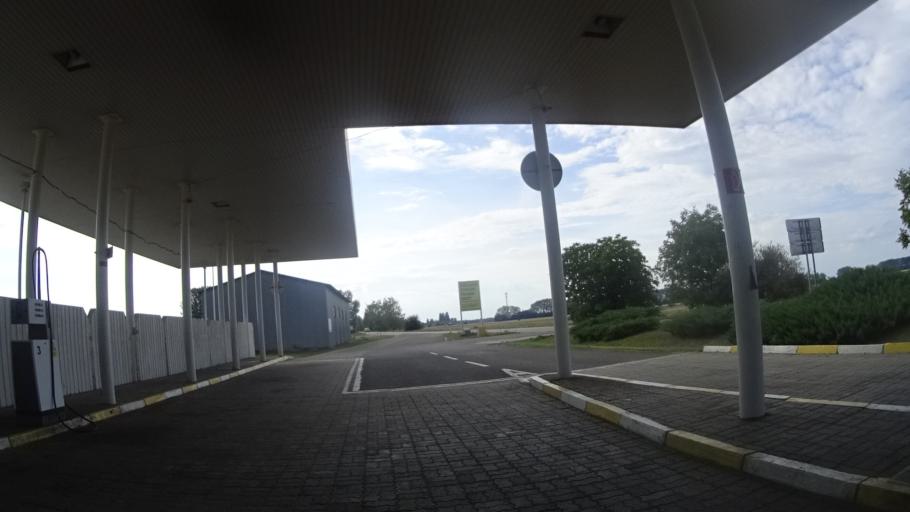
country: SK
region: Trnavsky
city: Gabcikovo
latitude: 47.9110
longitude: 17.5263
